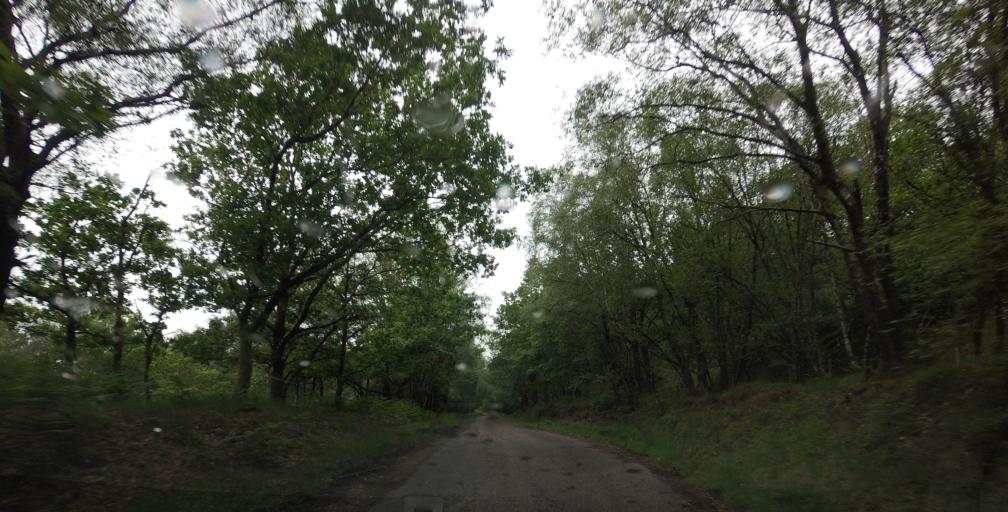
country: GB
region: Scotland
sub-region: Highland
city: Fort William
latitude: 56.8087
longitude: -5.1488
